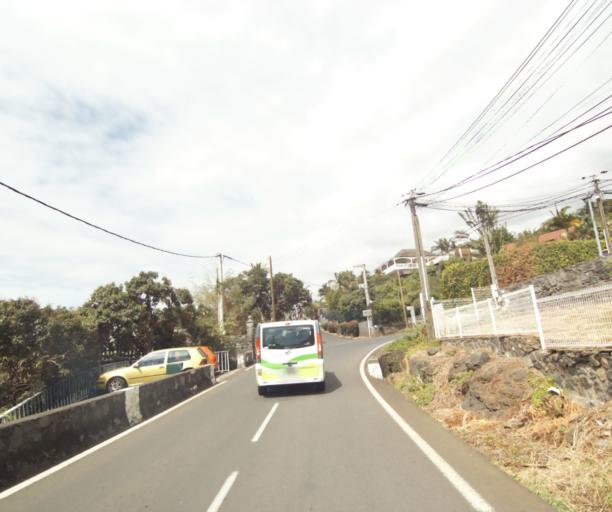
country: RE
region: Reunion
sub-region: Reunion
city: Saint-Paul
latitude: -21.0154
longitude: 55.2857
